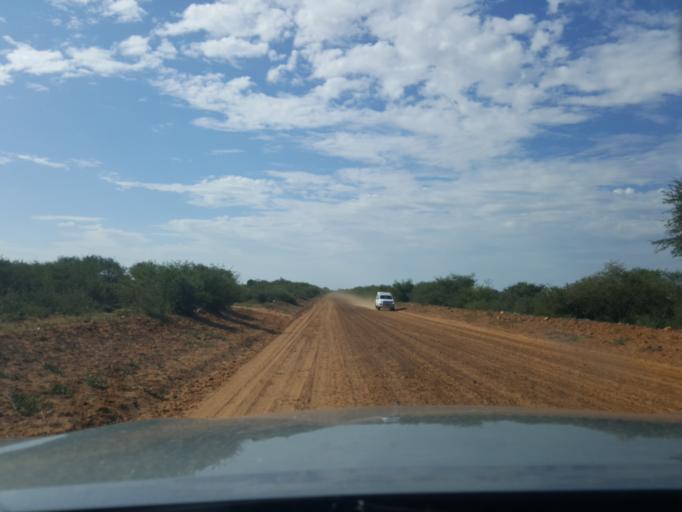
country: BW
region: Kweneng
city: Khudumelapye
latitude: -23.6234
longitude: 24.7272
